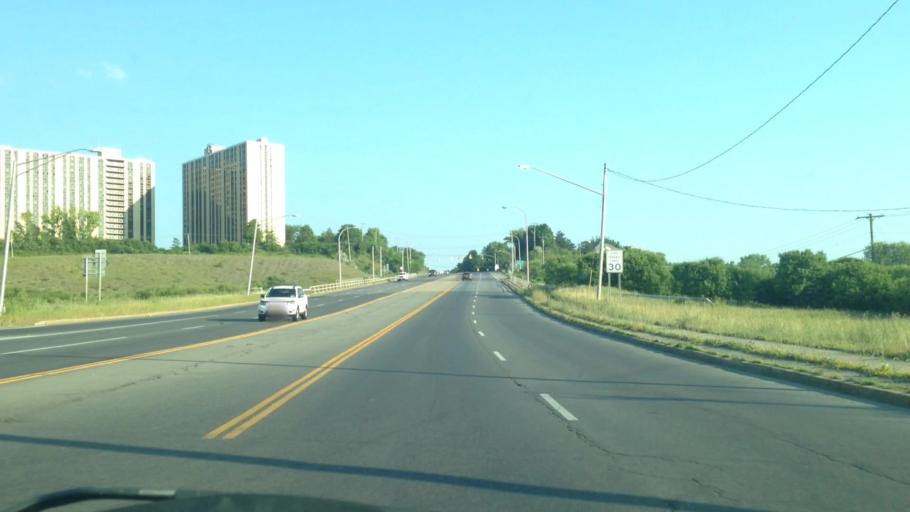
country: US
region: New York
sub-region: Onondaga County
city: Nedrow
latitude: 43.0089
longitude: -76.1327
